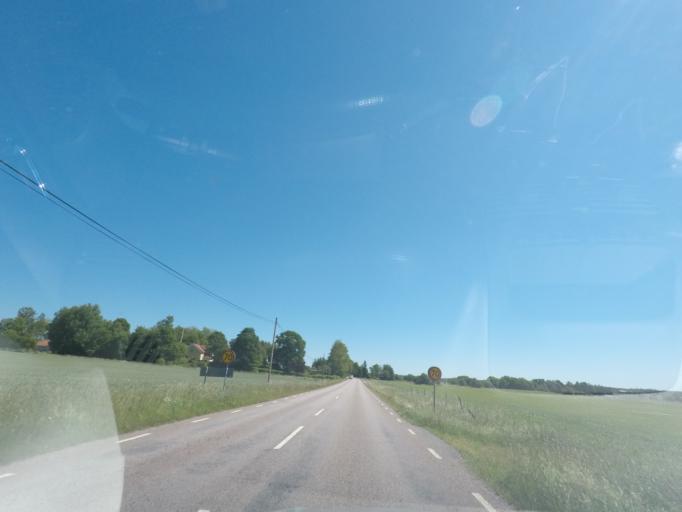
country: SE
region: Vaestmanland
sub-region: Vasteras
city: Tillberga
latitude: 59.6768
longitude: 16.7350
